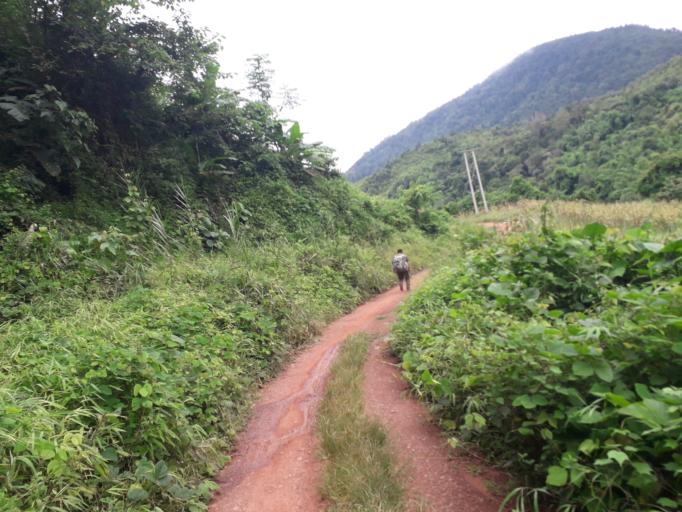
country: CN
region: Yunnan
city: Menglie
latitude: 22.2237
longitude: 101.6432
